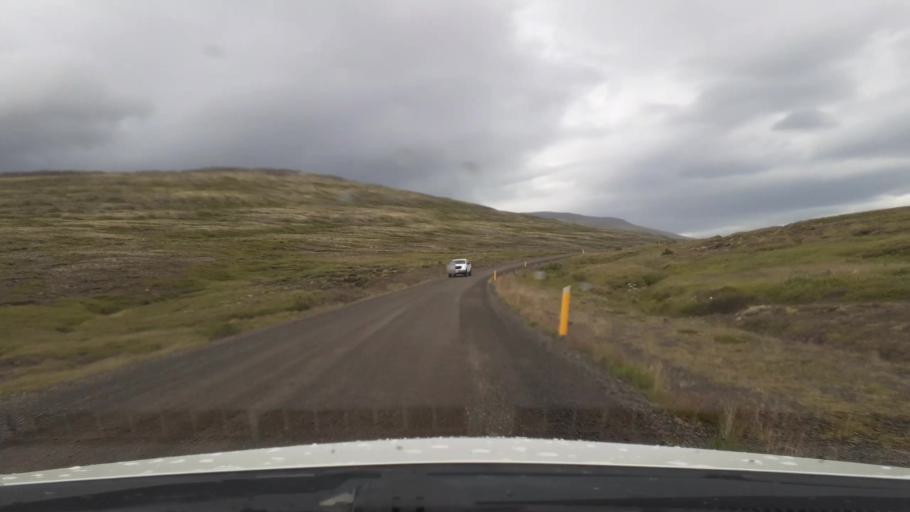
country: IS
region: Capital Region
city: Mosfellsbaer
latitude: 64.4861
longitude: -21.5143
